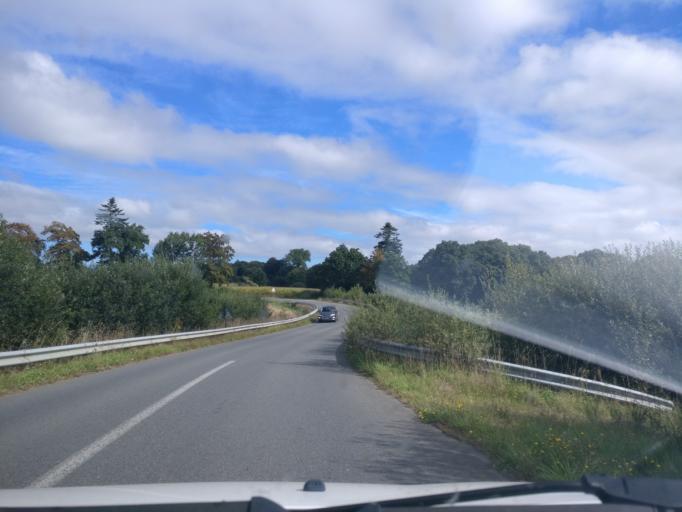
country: FR
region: Brittany
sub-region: Departement des Cotes-d'Armor
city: Rospez
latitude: 48.7163
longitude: -3.3978
